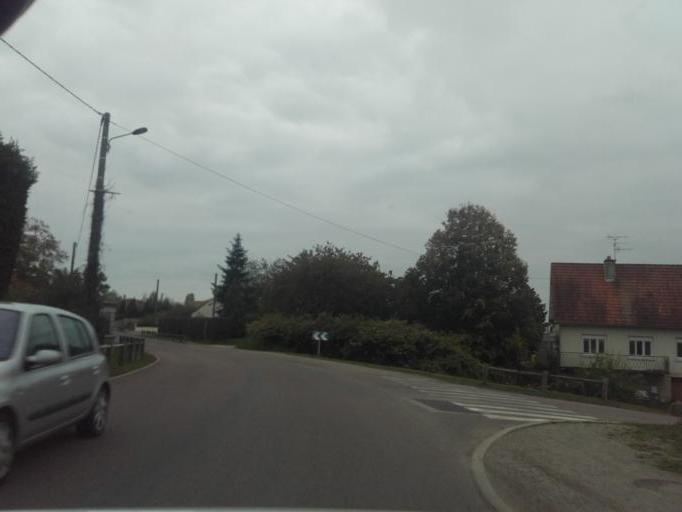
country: FR
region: Bourgogne
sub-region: Departement de Saone-et-Loire
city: Chagny
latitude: 46.9129
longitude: 4.7827
